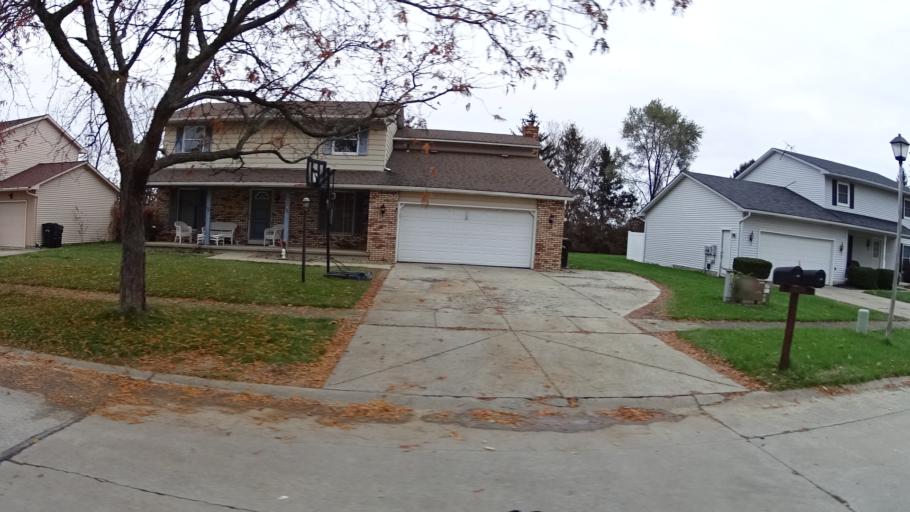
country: US
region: Ohio
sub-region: Lorain County
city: Sheffield
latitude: 41.4164
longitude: -82.0895
